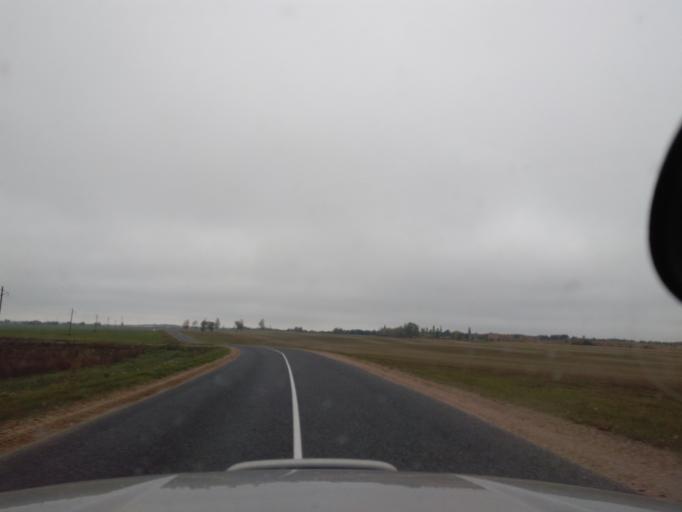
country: BY
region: Minsk
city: Kapyl'
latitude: 53.1544
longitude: 27.1803
